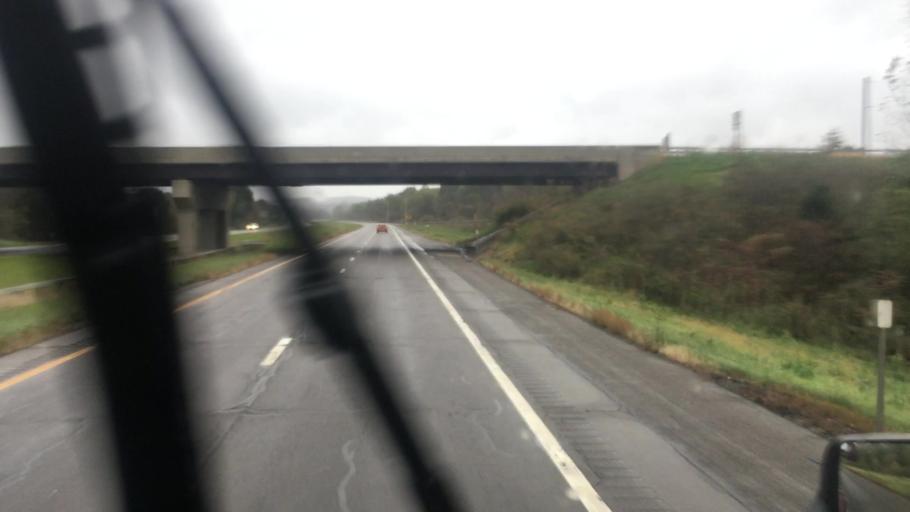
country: US
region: New York
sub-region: Tioga County
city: Apalachin
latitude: 42.0653
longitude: -76.1454
